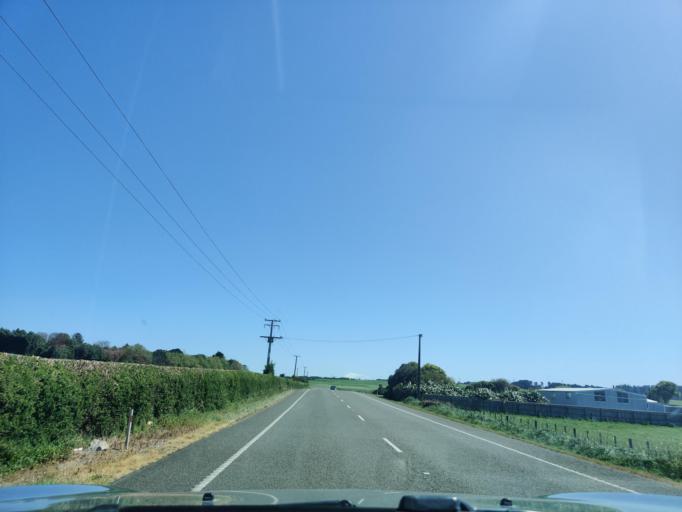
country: NZ
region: Taranaki
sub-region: South Taranaki District
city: Patea
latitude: -39.7804
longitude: 174.6923
